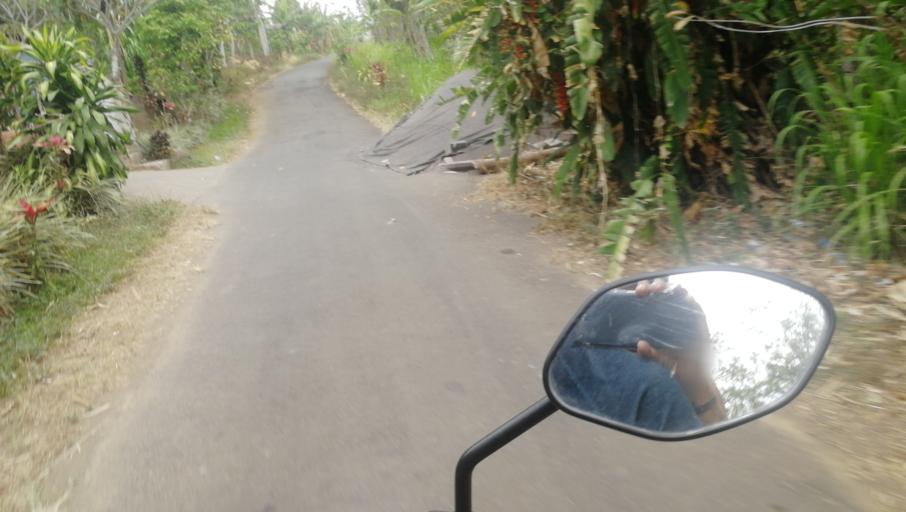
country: ID
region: Bali
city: Banjar Ambengan
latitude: -8.2107
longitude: 115.1107
